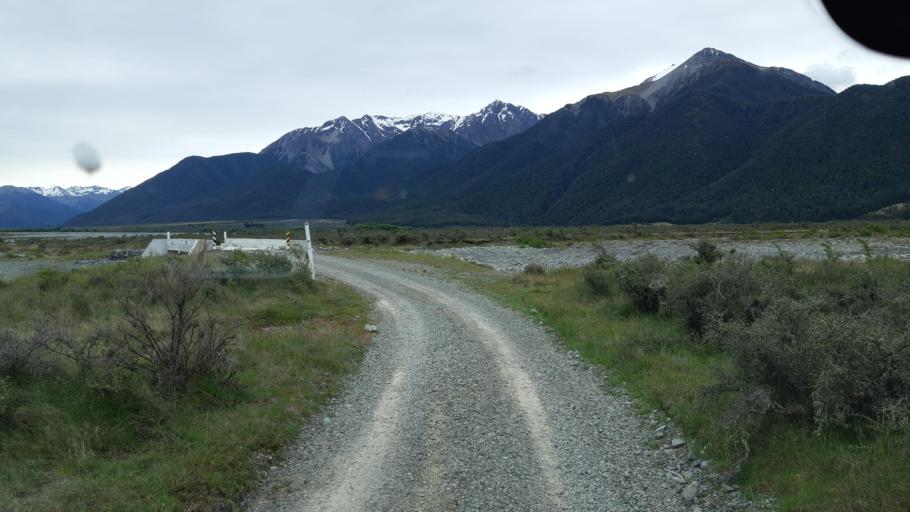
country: NZ
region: Canterbury
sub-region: Waimakariri District
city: Oxford
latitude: -43.0042
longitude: 171.7485
